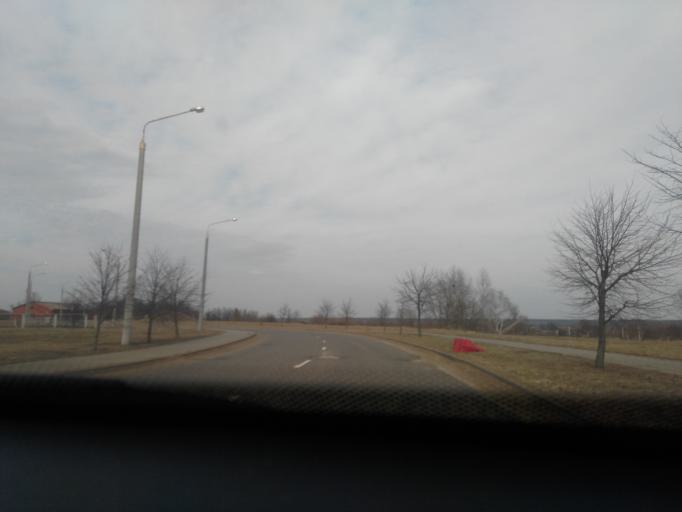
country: BY
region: Mogilev
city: Babruysk
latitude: 53.1420
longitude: 29.2508
